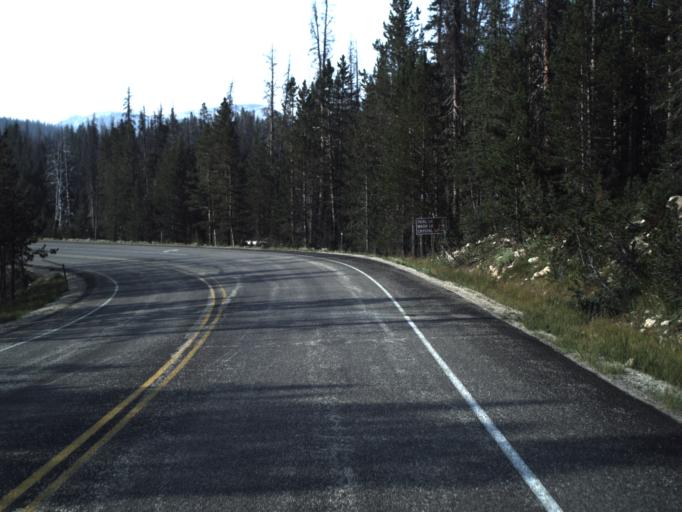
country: US
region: Utah
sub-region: Summit County
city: Kamas
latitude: 40.6766
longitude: -110.9513
